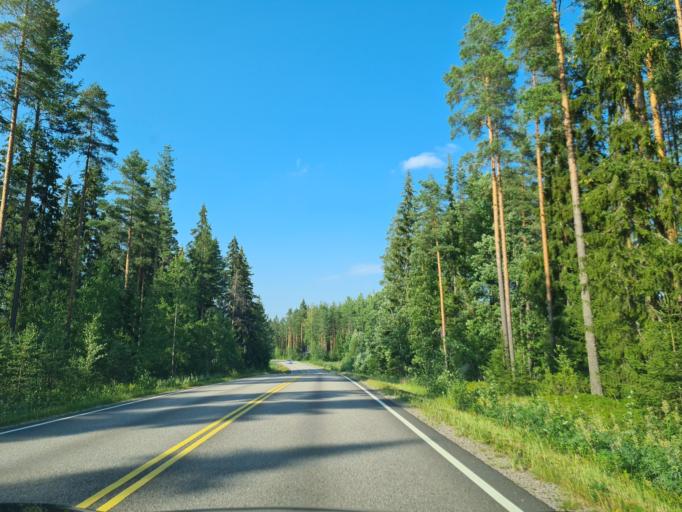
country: FI
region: Satakunta
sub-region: Pohjois-Satakunta
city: Karvia
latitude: 62.2030
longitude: 22.5991
